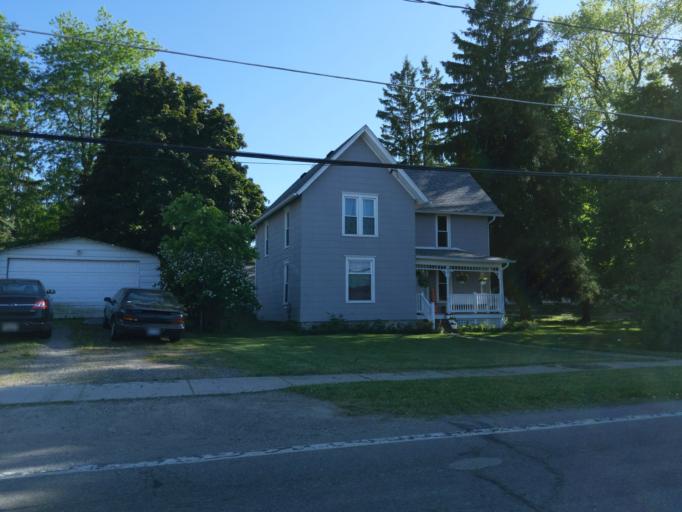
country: US
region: Michigan
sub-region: Ingham County
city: Stockbridge
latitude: 42.4523
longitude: -84.1839
